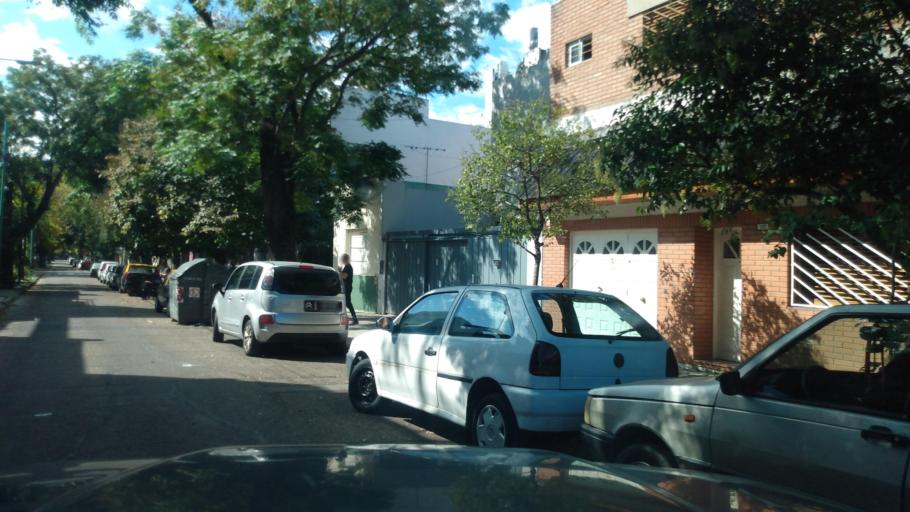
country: AR
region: Buenos Aires F.D.
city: Villa Santa Rita
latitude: -34.5865
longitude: -58.4832
